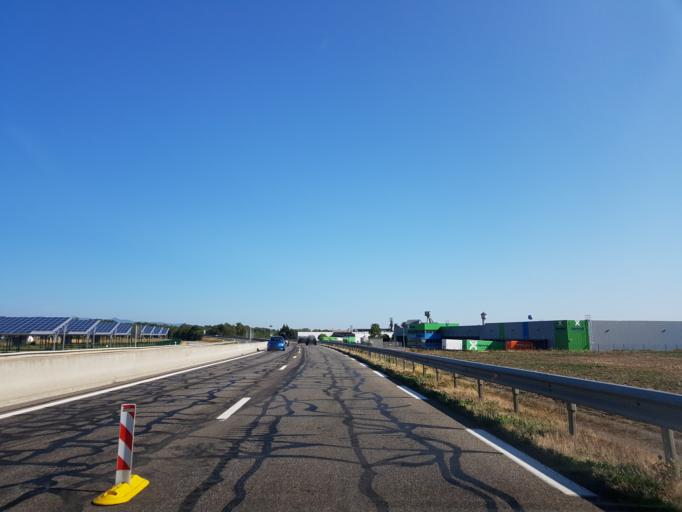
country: FR
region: Alsace
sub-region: Departement du Haut-Rhin
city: Pulversheim
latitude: 47.8380
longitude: 7.2767
